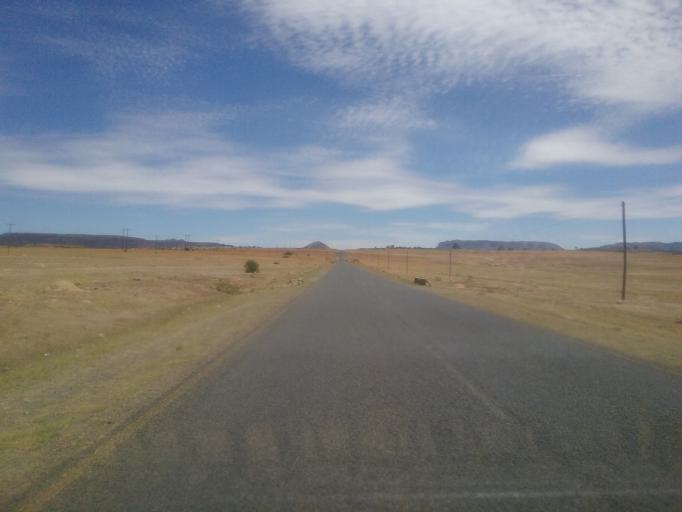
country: LS
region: Mohale's Hoek District
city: Mohale's Hoek
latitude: -30.0083
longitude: 27.3504
